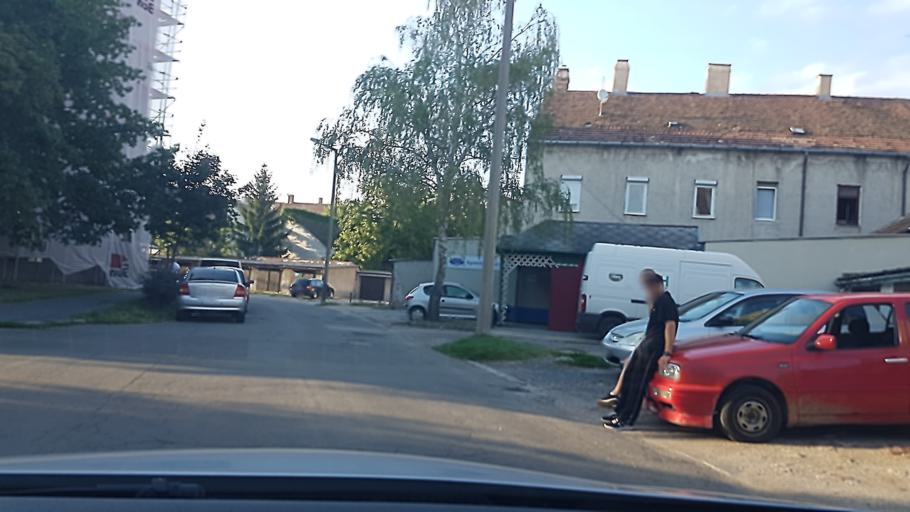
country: HU
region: Gyor-Moson-Sopron
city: Sopron
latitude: 47.6803
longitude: 16.5928
